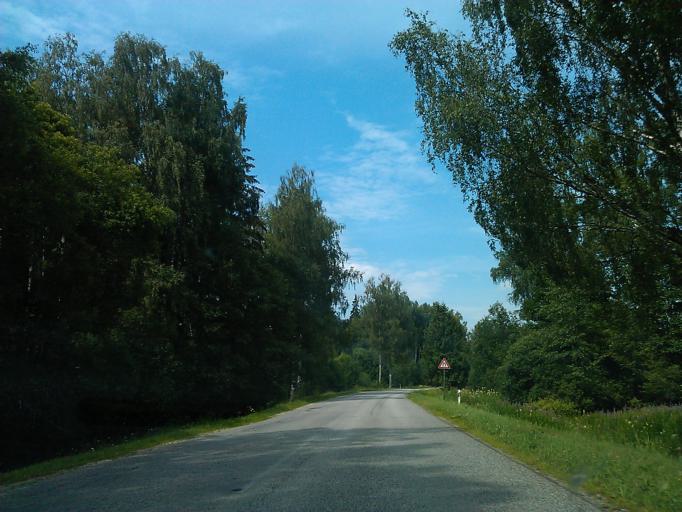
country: LV
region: Burtnieki
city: Matisi
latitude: 57.6715
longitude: 25.2031
